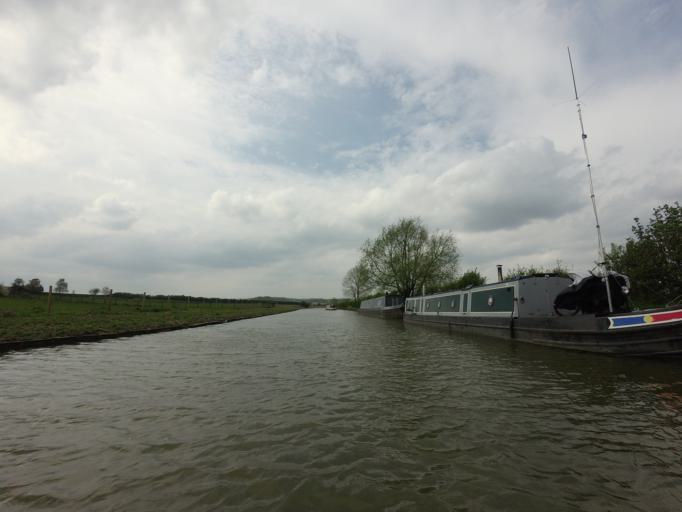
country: GB
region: England
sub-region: Central Bedfordshire
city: Leighton Buzzard
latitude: 51.8943
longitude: -0.6637
